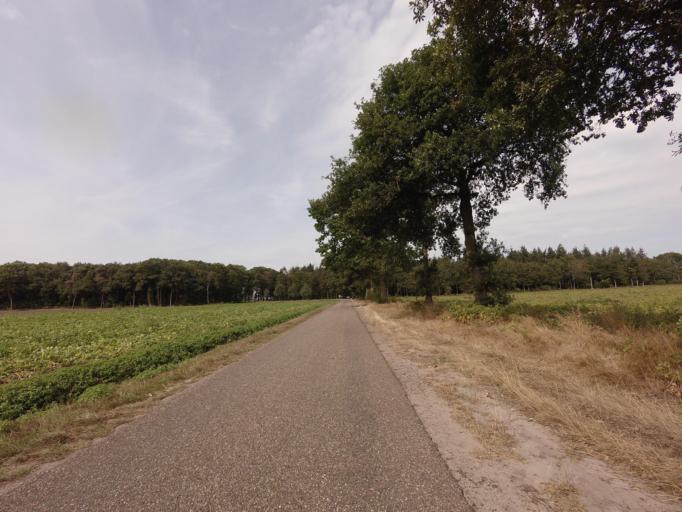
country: NL
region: North Brabant
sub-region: Gemeente Sint Anthonis
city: Sint Anthonis
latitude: 51.5572
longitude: 5.8153
